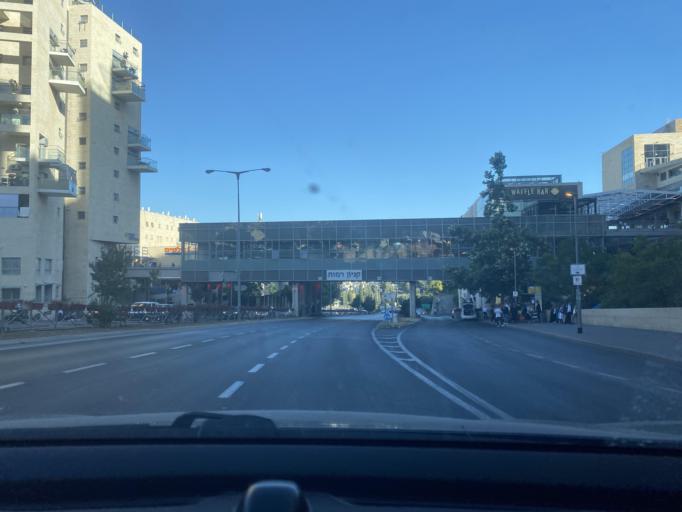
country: PS
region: West Bank
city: Bayt Iksa
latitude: 31.8180
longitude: 35.1948
